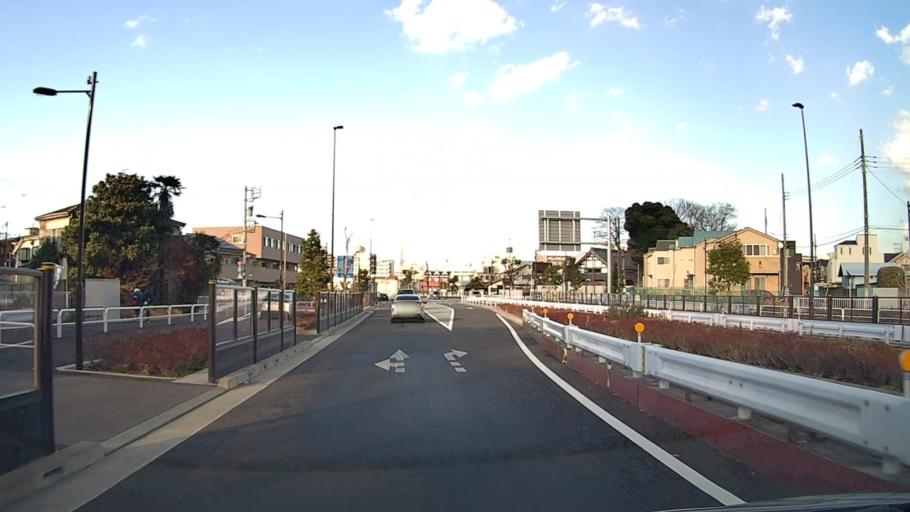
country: JP
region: Saitama
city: Wako
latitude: 35.7633
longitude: 139.6530
